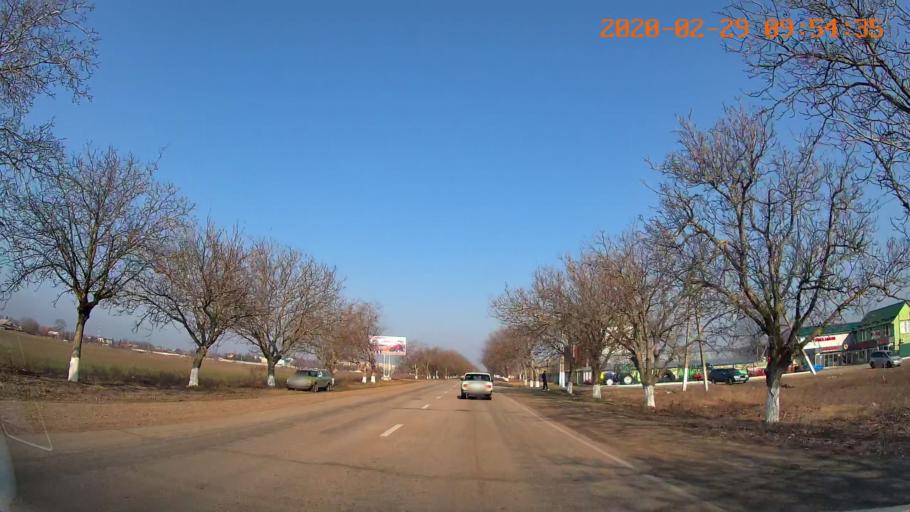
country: MD
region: Telenesti
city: Slobozia
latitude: 46.7296
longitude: 29.7149
